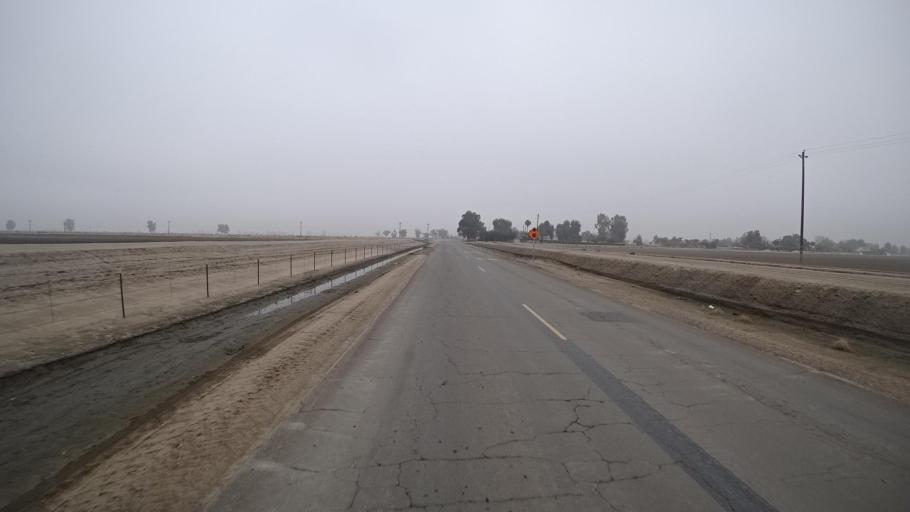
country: US
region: California
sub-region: Kern County
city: Greenfield
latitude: 35.2373
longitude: -119.0233
